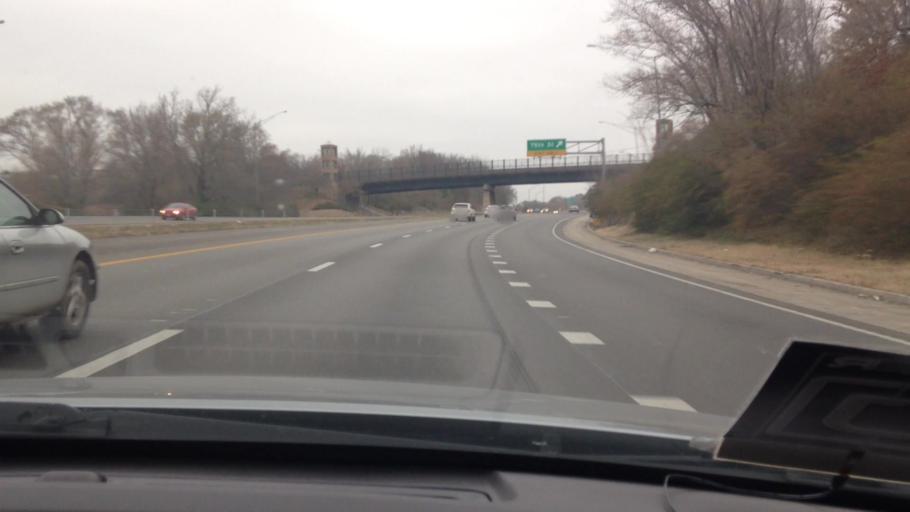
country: US
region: Kansas
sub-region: Johnson County
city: Leawood
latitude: 38.9853
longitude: -94.5512
